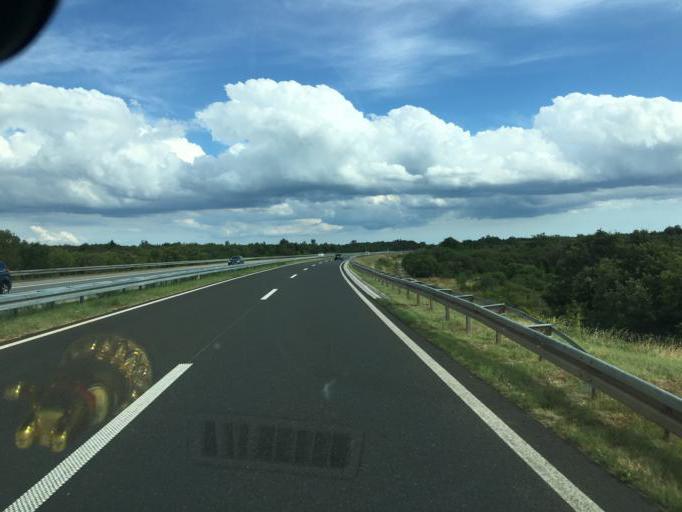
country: HR
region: Istarska
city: Vodnjan
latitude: 45.0863
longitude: 13.8353
